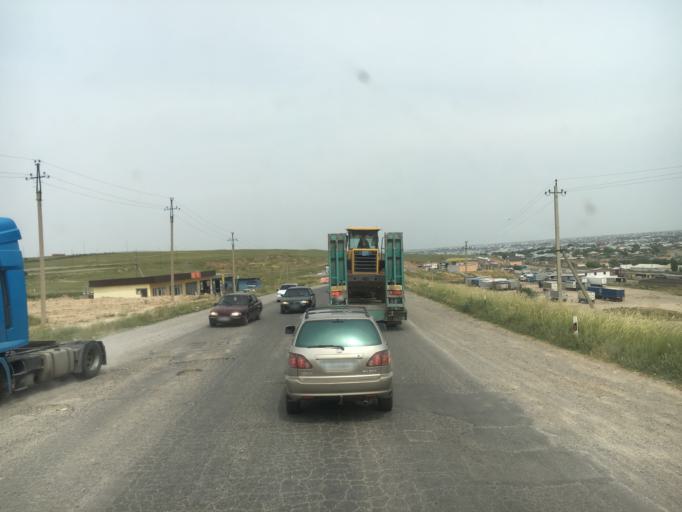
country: KZ
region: Ongtustik Qazaqstan
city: Shymkent
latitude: 42.3246
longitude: 69.5147
